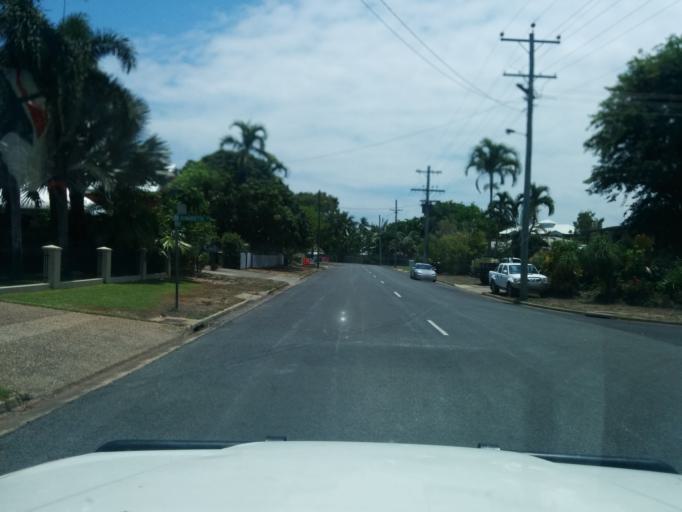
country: AU
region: Queensland
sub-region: Cairns
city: Yorkeys Knob
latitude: -16.8370
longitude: 145.7386
